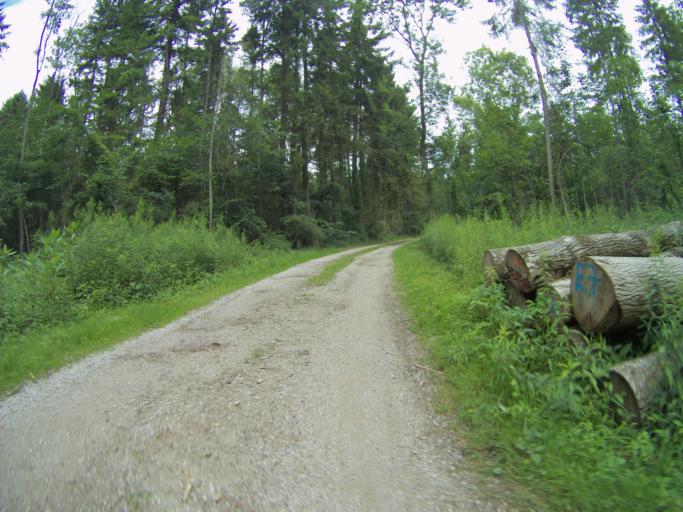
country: DE
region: Bavaria
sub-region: Upper Bavaria
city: Freising
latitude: 48.3726
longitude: 11.7391
